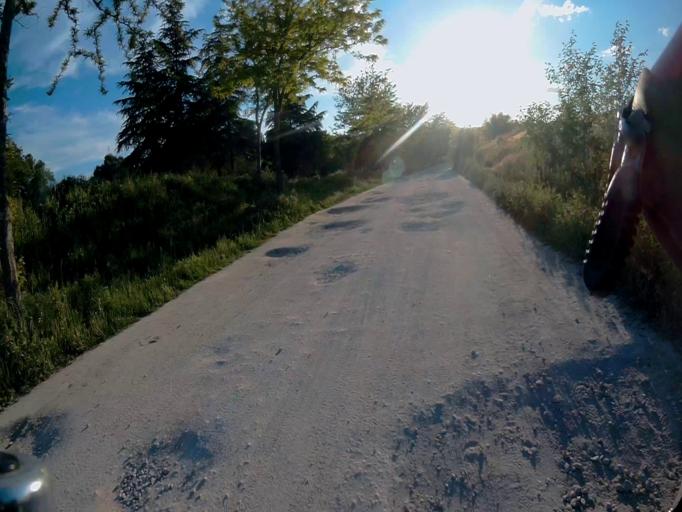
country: ES
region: Madrid
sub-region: Provincia de Madrid
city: Leganes
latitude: 40.3259
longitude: -3.7911
